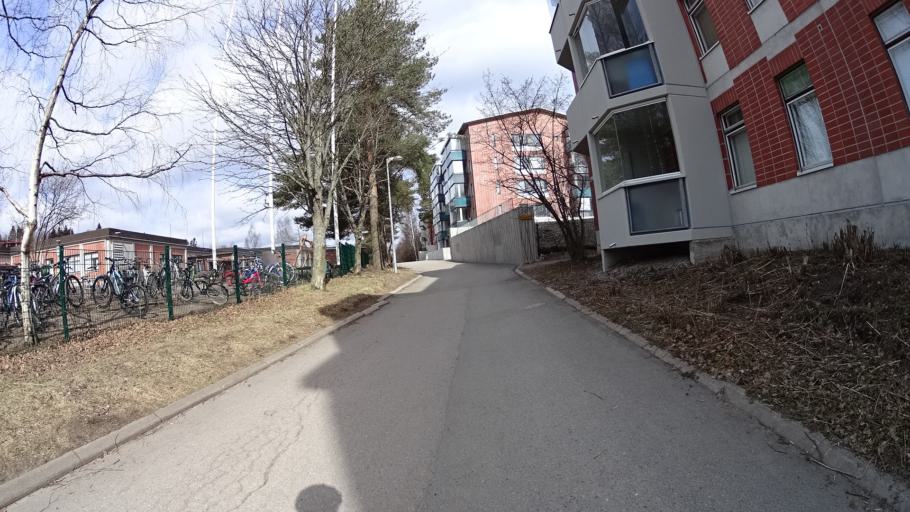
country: FI
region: Uusimaa
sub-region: Helsinki
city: Kilo
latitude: 60.2568
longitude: 24.8071
